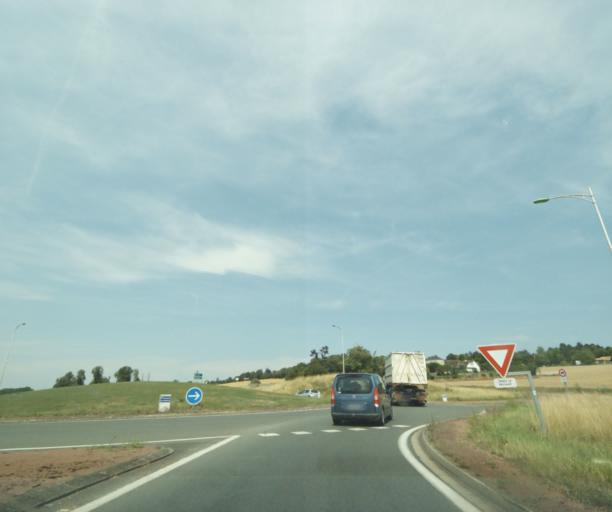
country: FR
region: Poitou-Charentes
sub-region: Departement de la Vienne
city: Chatellerault
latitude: 46.8073
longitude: 0.5660
